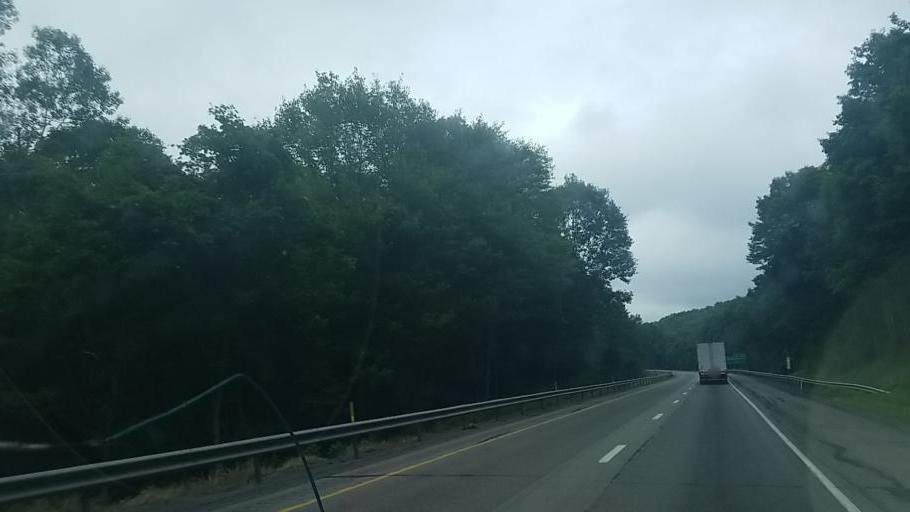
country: US
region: Pennsylvania
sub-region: Jefferson County
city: Brookville
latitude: 41.1443
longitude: -78.9896
